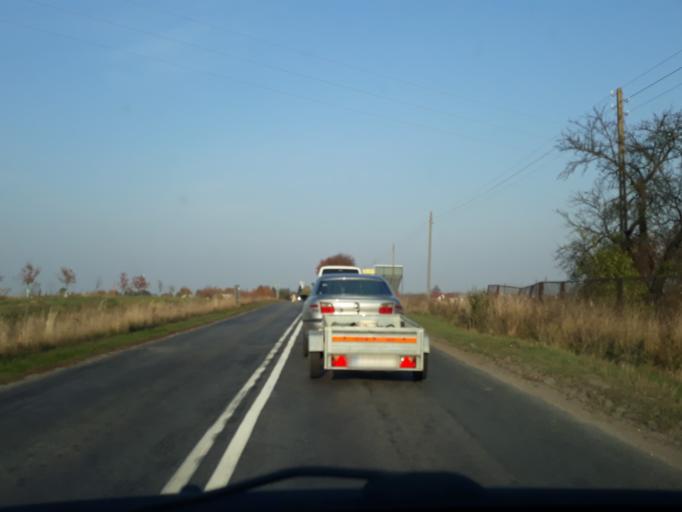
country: PL
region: Pomeranian Voivodeship
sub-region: Powiat chojnicki
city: Chojnice
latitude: 53.6747
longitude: 17.5317
